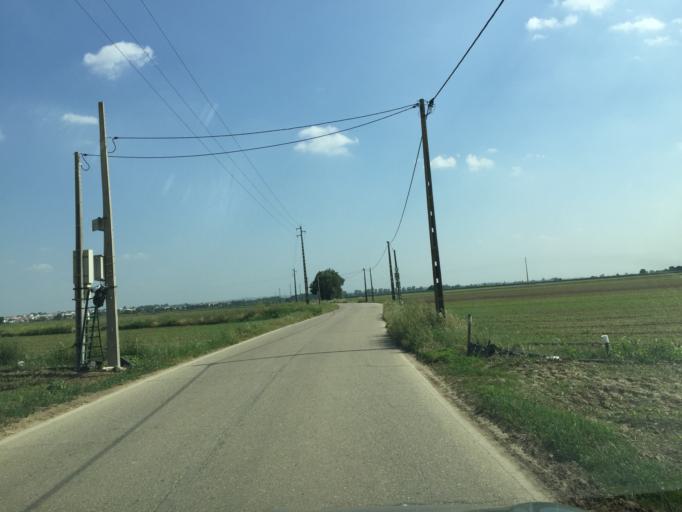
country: PT
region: Santarem
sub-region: Alpiarca
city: Alpiarca
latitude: 39.2801
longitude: -8.5941
